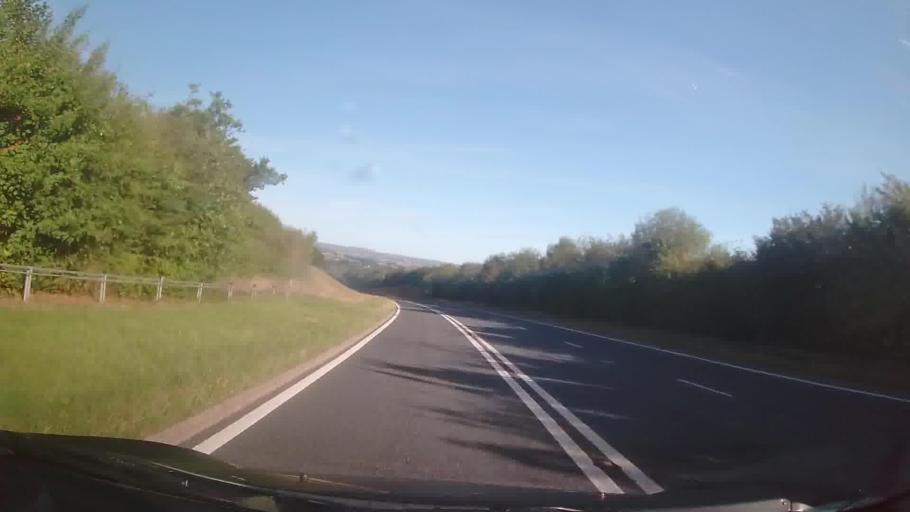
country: GB
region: Wales
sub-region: Sir Powys
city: Hay
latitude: 51.9893
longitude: -3.2335
